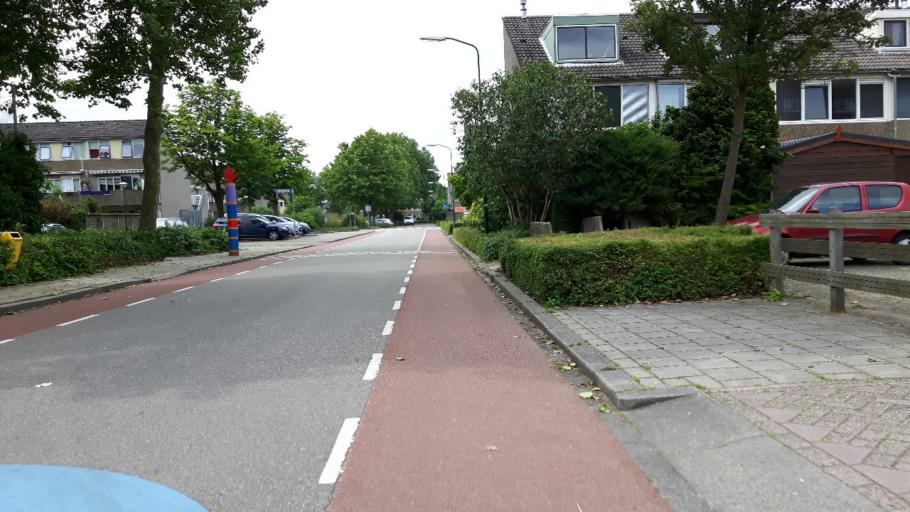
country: NL
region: Utrecht
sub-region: Stichtse Vecht
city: Maarssen
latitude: 52.1274
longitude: 5.0335
